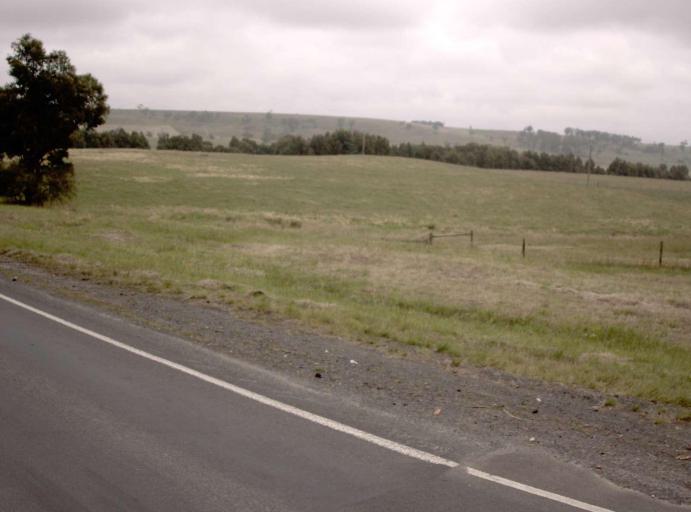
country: AU
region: Victoria
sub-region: Latrobe
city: Traralgon
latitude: -38.2491
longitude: 146.5469
